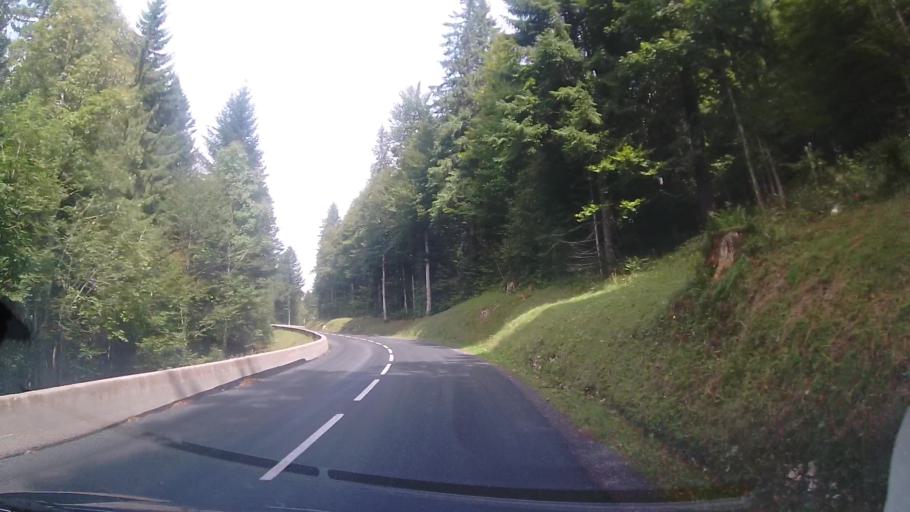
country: FR
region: Rhone-Alpes
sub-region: Departement de l'Ain
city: Gex
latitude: 46.3861
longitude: 6.0438
